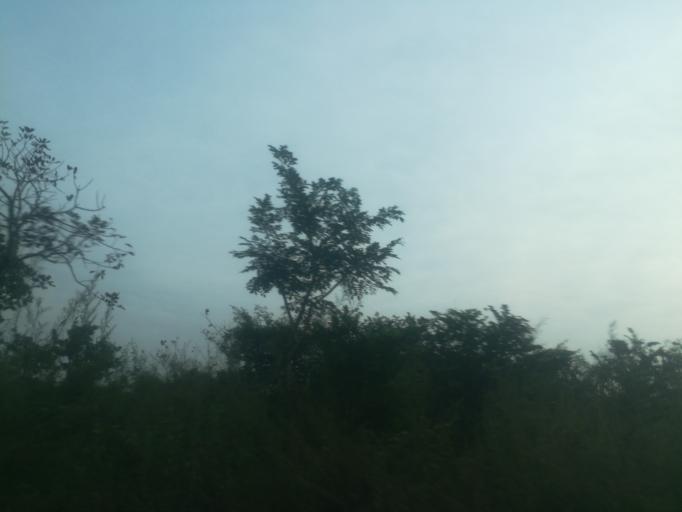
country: NG
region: Ogun
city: Abeokuta
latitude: 7.1984
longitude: 3.2240
